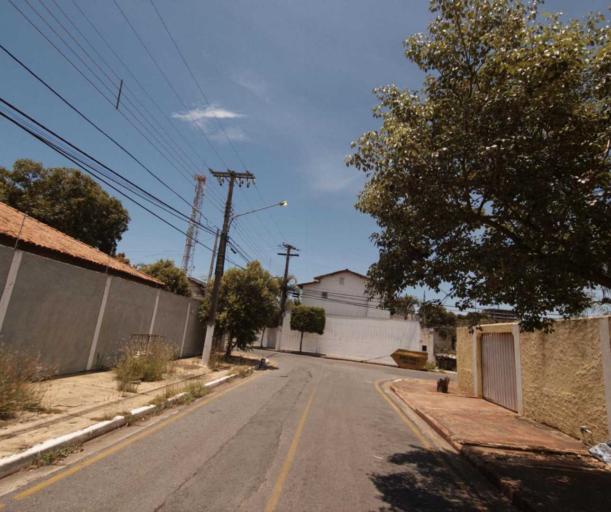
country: BR
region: Mato Grosso
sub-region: Cuiaba
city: Cuiaba
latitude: -15.6063
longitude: -56.1251
